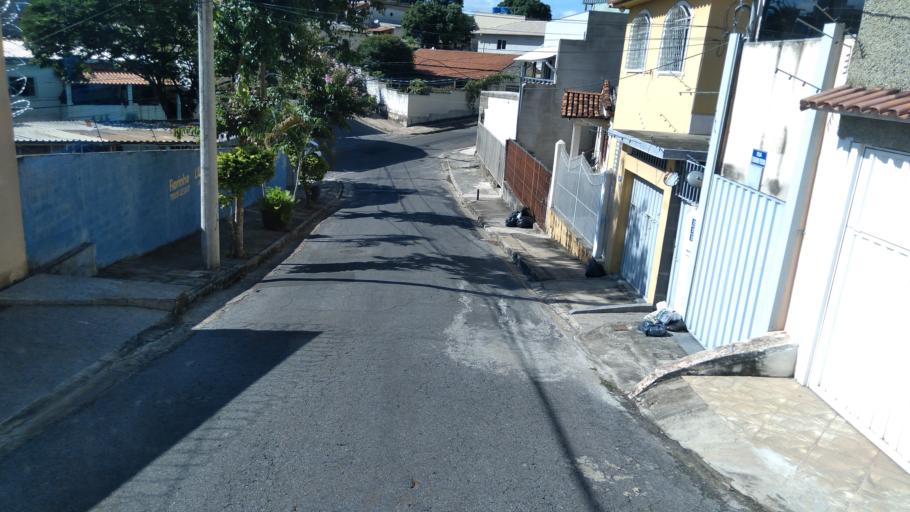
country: BR
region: Minas Gerais
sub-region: Belo Horizonte
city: Belo Horizonte
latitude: -19.8798
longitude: -43.9199
